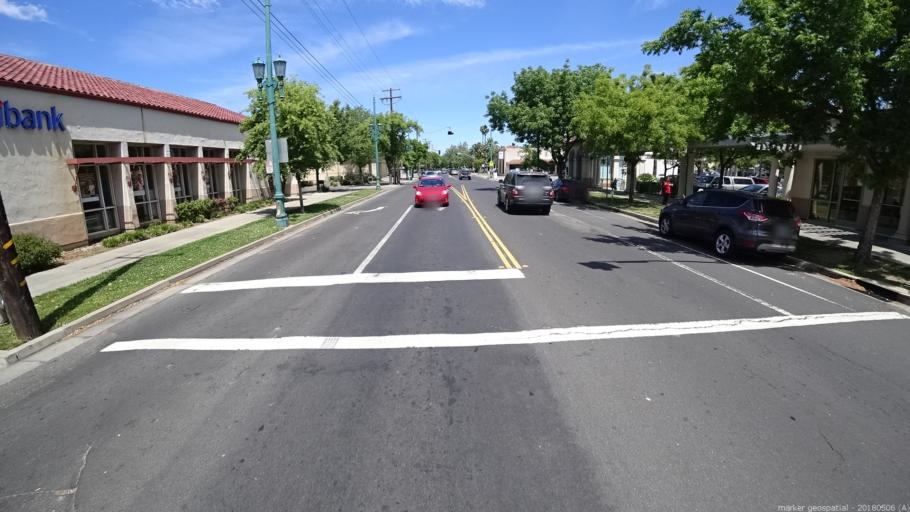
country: US
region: California
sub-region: Sacramento County
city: Sacramento
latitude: 38.5707
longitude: -121.4662
